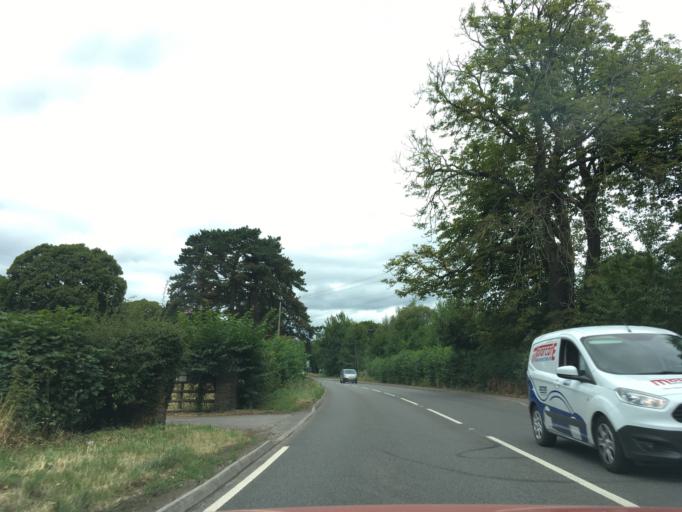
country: GB
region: Wales
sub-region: Monmouthshire
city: Abergavenny
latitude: 51.8061
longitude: -3.0082
